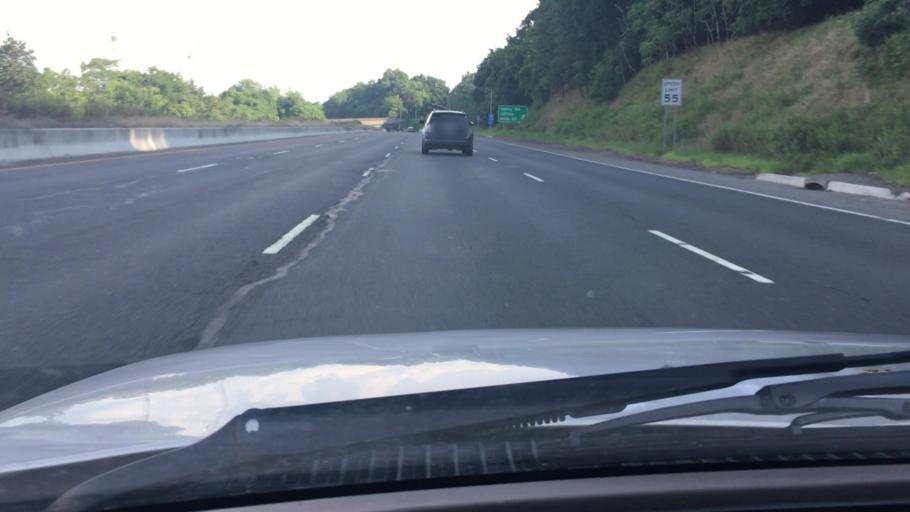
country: US
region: New Jersey
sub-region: Passaic County
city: Paterson
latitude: 40.9027
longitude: -74.1716
